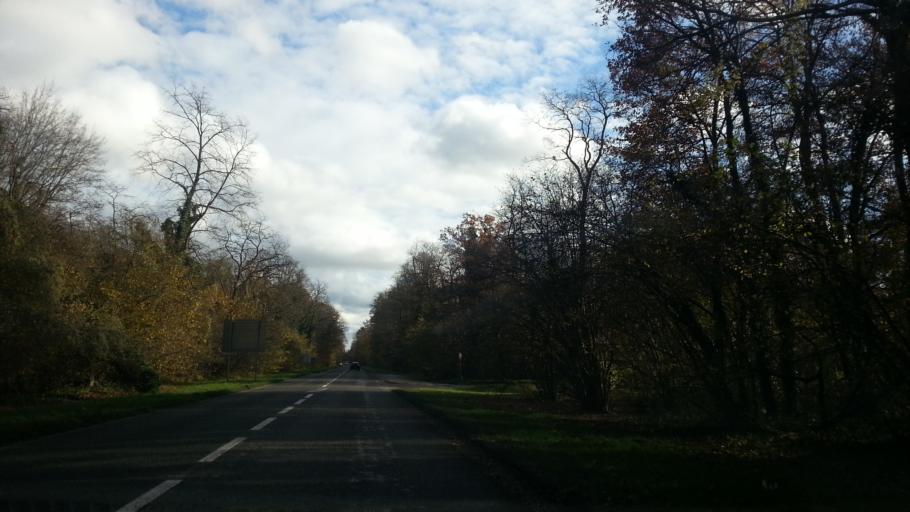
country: FR
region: Picardie
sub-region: Departement de l'Oise
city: Saint-Maximin
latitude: 49.2105
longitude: 2.4463
